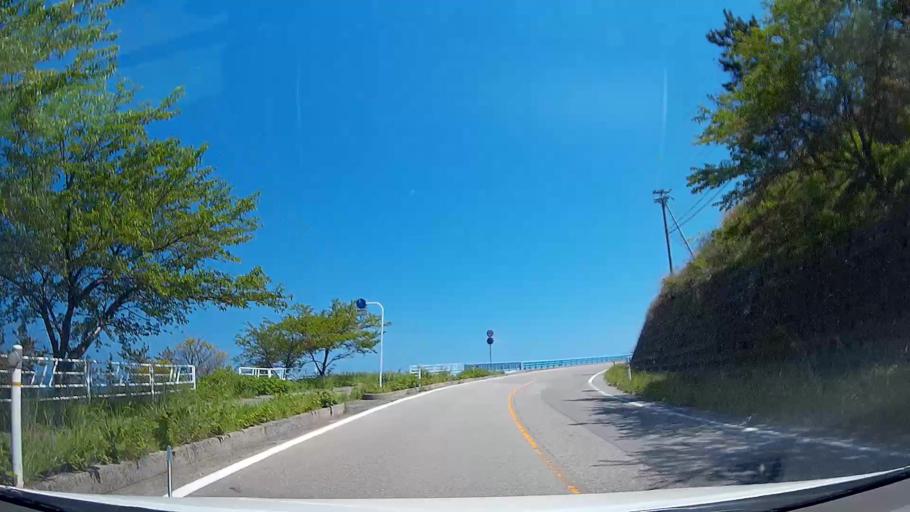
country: JP
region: Ishikawa
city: Nanao
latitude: 37.4159
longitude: 136.9796
